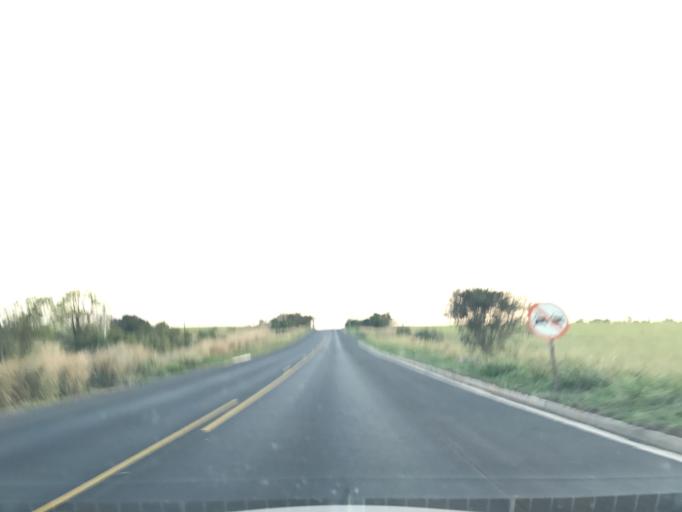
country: BR
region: Sao Paulo
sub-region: Pirapozinho
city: Pirapozinho
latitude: -22.4084
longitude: -51.6282
